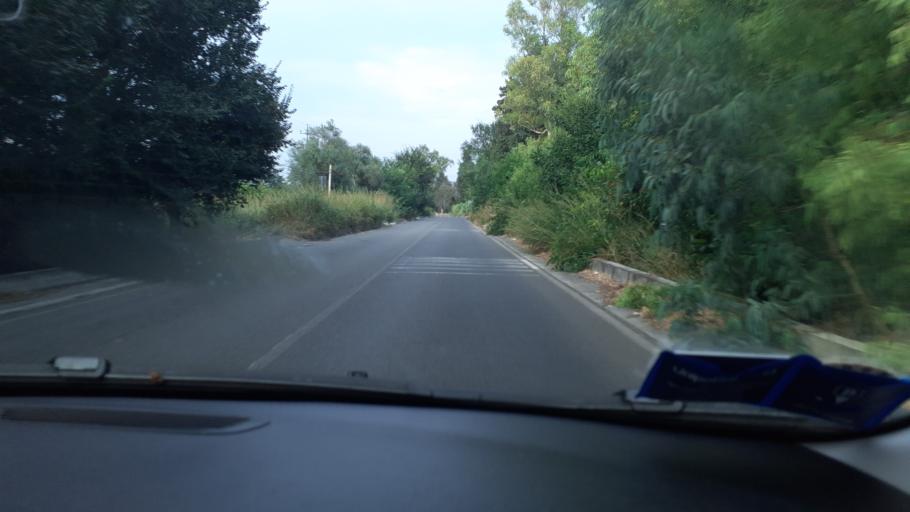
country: IT
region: Sicily
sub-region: Catania
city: Catania
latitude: 37.4523
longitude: 15.0258
